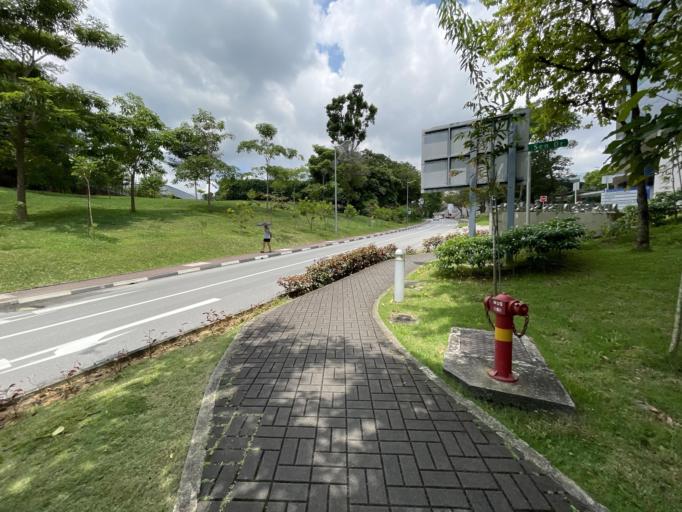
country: SG
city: Singapore
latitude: 1.2925
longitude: 103.7737
